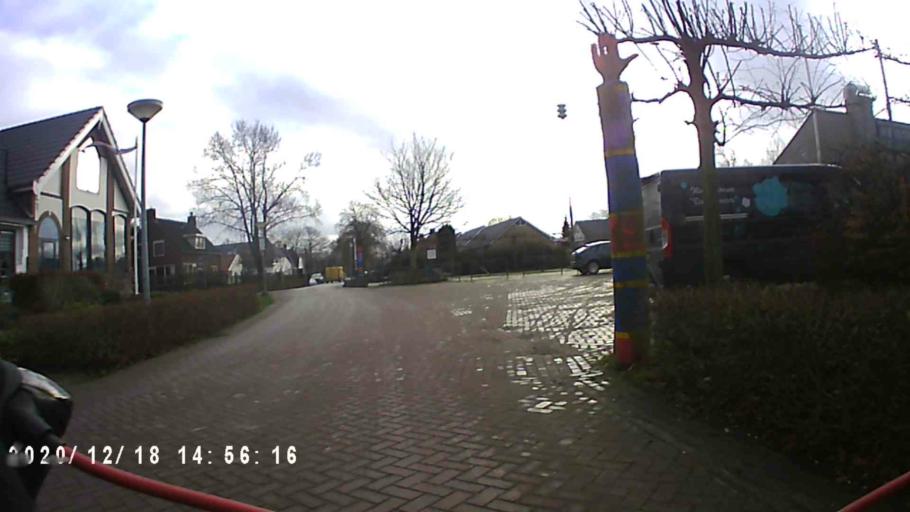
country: NL
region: Groningen
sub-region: Gemeente Haren
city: Haren
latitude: 53.1840
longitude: 6.6862
